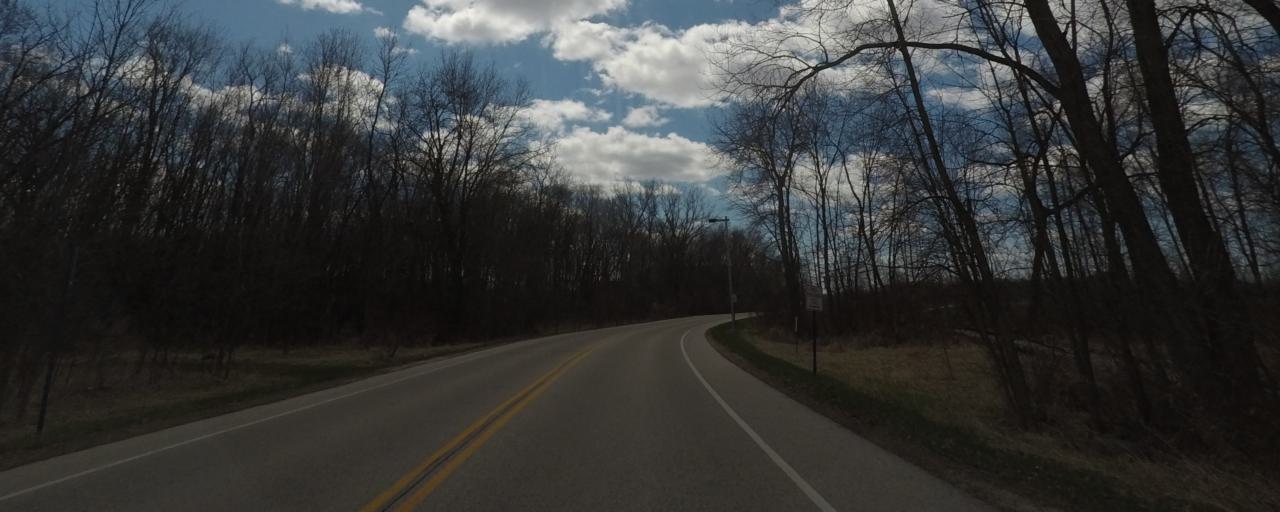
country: US
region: Wisconsin
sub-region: Waukesha County
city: Brookfield
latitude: 43.0821
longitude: -88.1580
